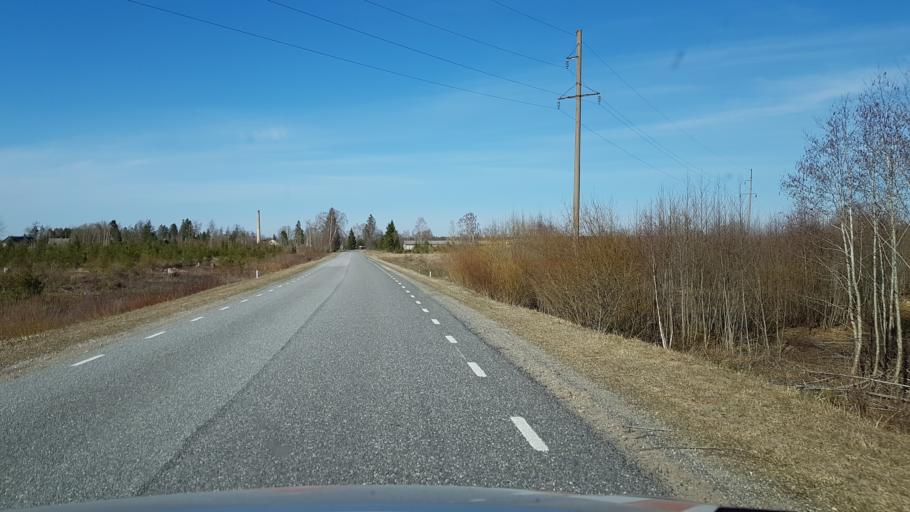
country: EE
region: Laeaene-Virumaa
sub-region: Rakke vald
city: Rakke
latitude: 58.9935
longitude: 26.2722
